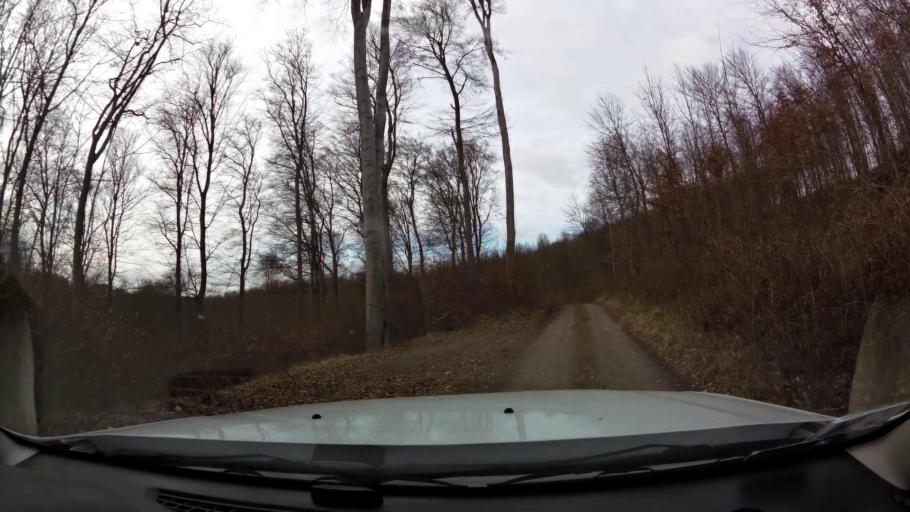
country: PL
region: West Pomeranian Voivodeship
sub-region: Powiat drawski
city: Drawsko Pomorskie
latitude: 53.5009
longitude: 15.7105
